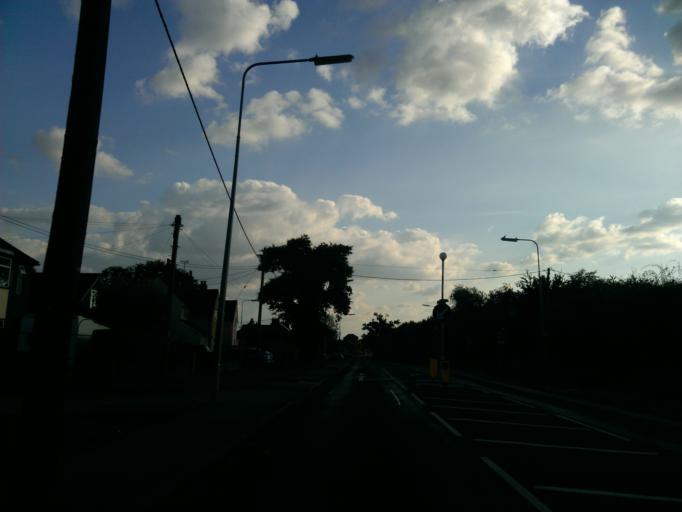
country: GB
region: England
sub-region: Essex
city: Braintree
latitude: 51.9060
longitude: 0.5742
